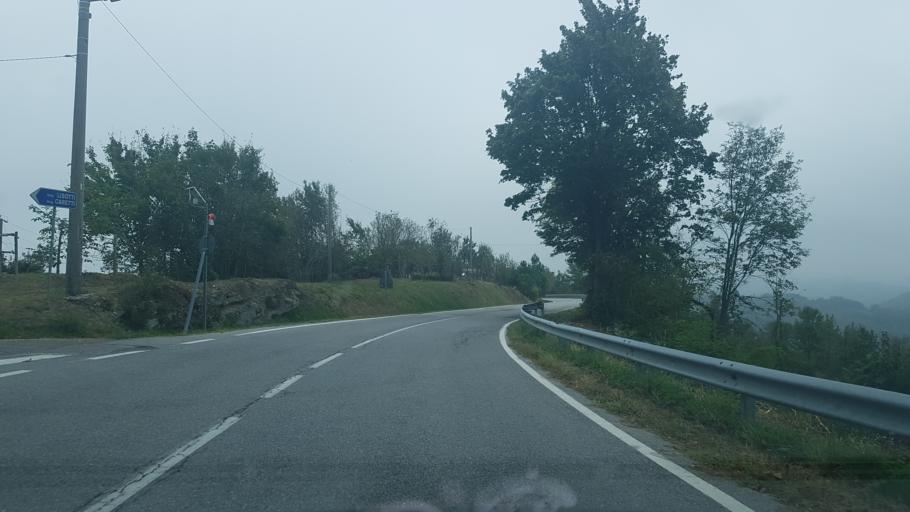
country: IT
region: Piedmont
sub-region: Provincia di Cuneo
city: Sale delle Langhe
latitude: 44.4082
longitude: 8.1063
